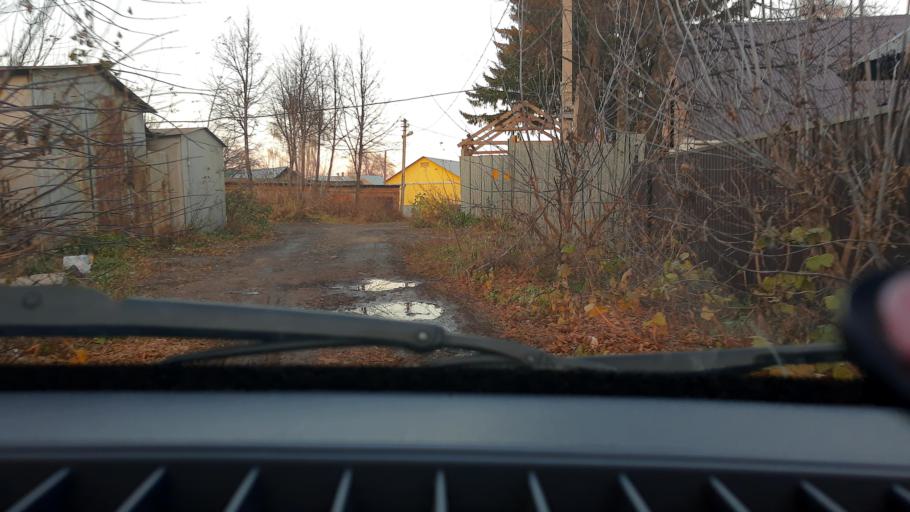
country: RU
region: Bashkortostan
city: Ufa
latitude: 54.7959
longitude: 56.1458
